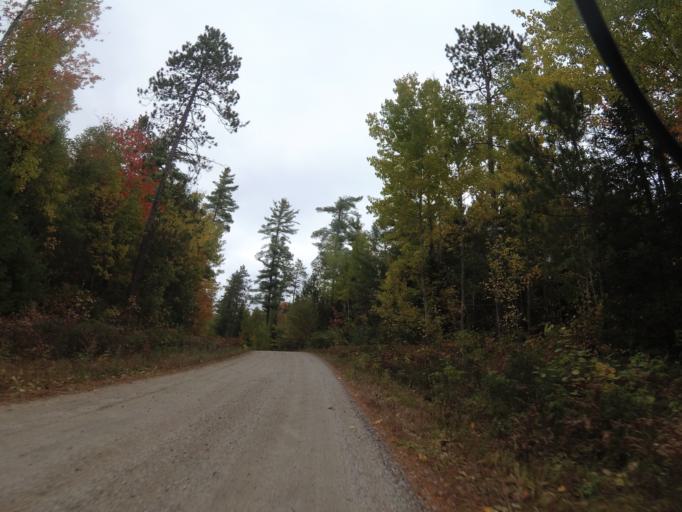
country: CA
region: Ontario
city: Renfrew
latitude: 45.2138
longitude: -77.0704
